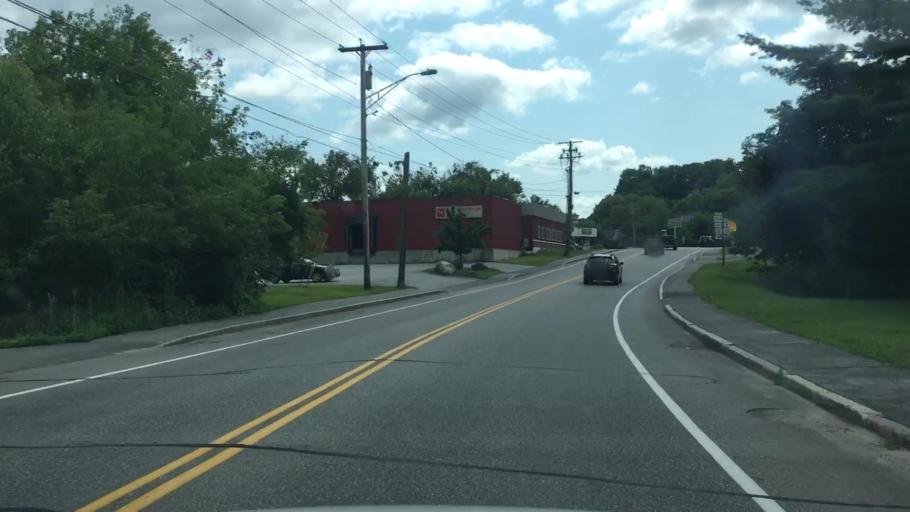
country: US
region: Maine
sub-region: Kennebec County
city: Augusta
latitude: 44.3226
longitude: -69.7751
